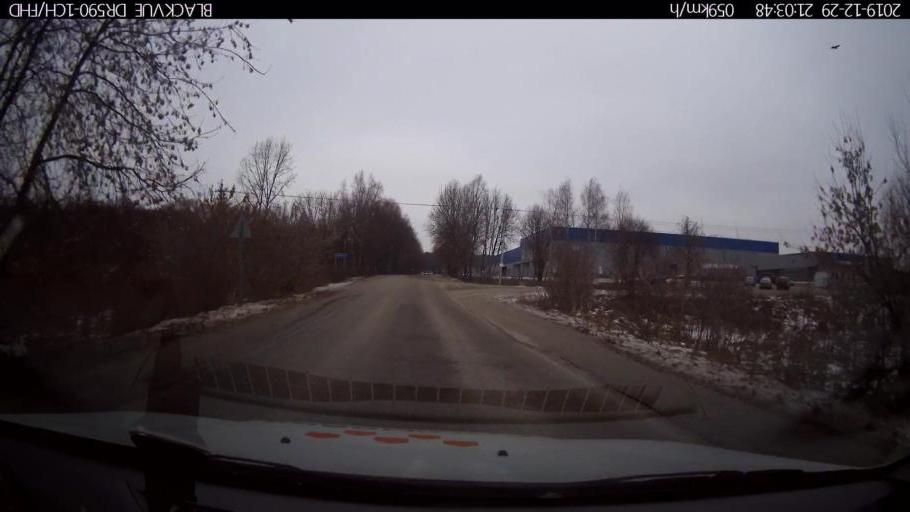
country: RU
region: Nizjnij Novgorod
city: Afonino
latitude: 56.1981
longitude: 44.0055
